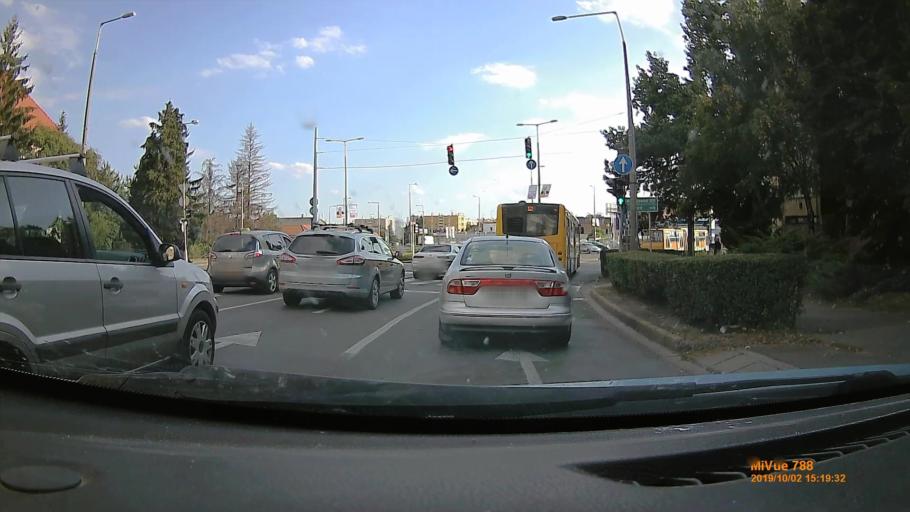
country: HU
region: Heves
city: Eger
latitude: 47.8919
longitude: 20.3786
